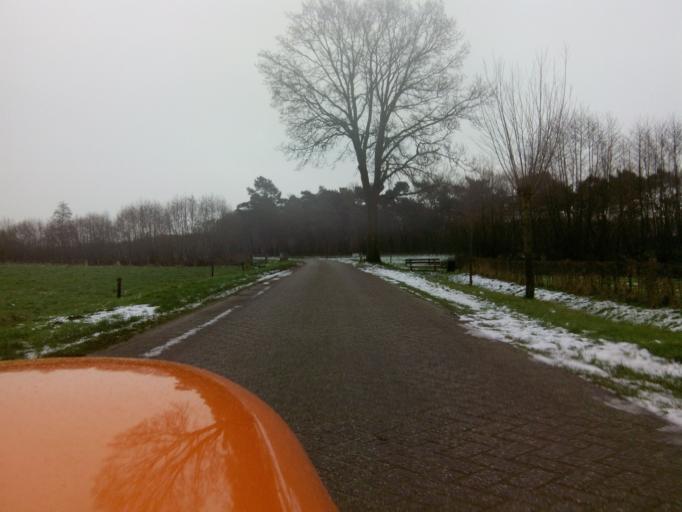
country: NL
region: Gelderland
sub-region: Gemeente Putten
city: Putten
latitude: 52.2377
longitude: 5.5480
